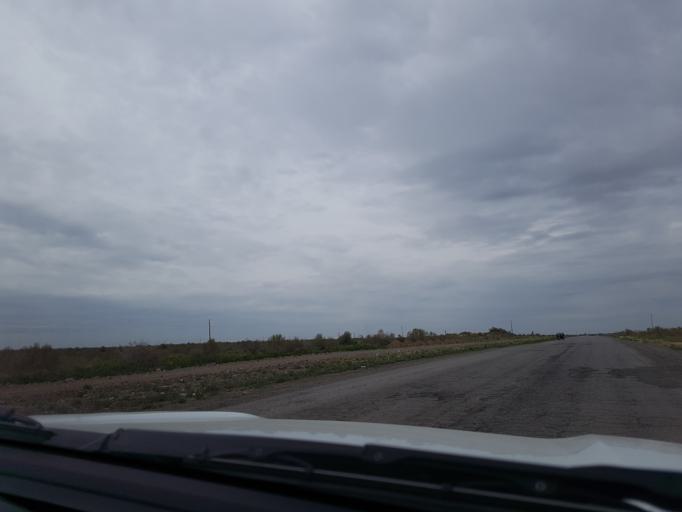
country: TM
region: Mary
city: Bayramaly
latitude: 37.8054
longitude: 62.5639
